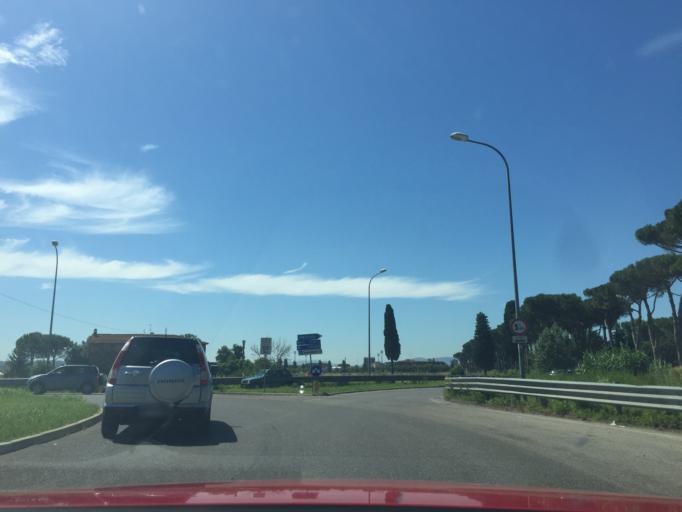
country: IT
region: Tuscany
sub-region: Province of Pisa
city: Pontedera
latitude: 43.6756
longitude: 10.6435
